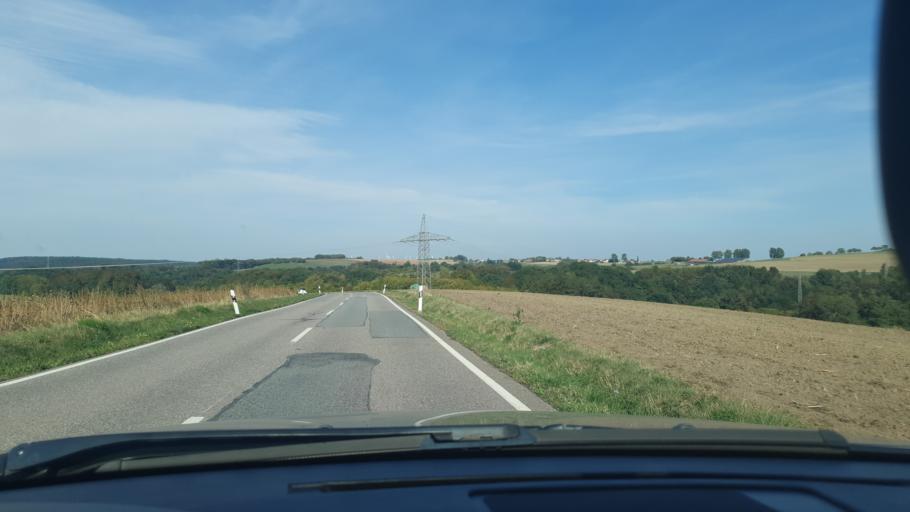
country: DE
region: Rheinland-Pfalz
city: Zweibrucken
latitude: 49.2880
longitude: 7.3680
